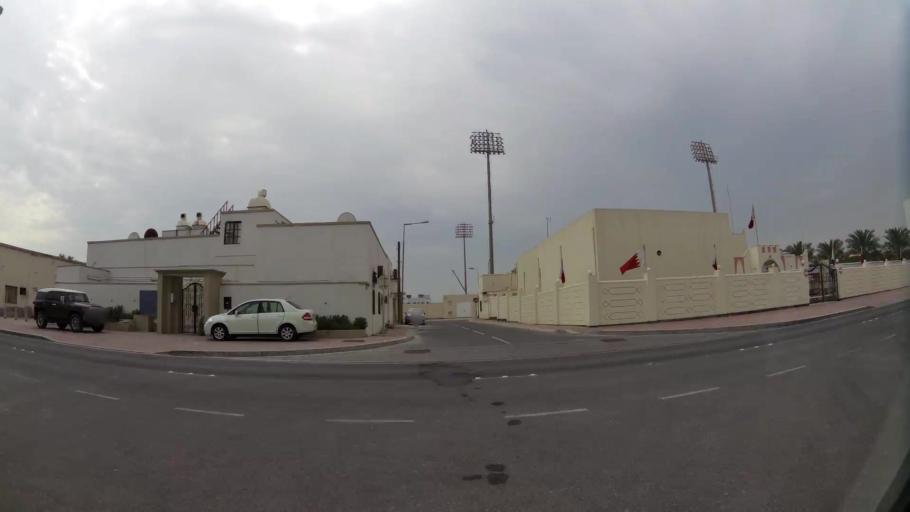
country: BH
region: Northern
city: Ar Rifa'
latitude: 26.0560
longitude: 50.6177
